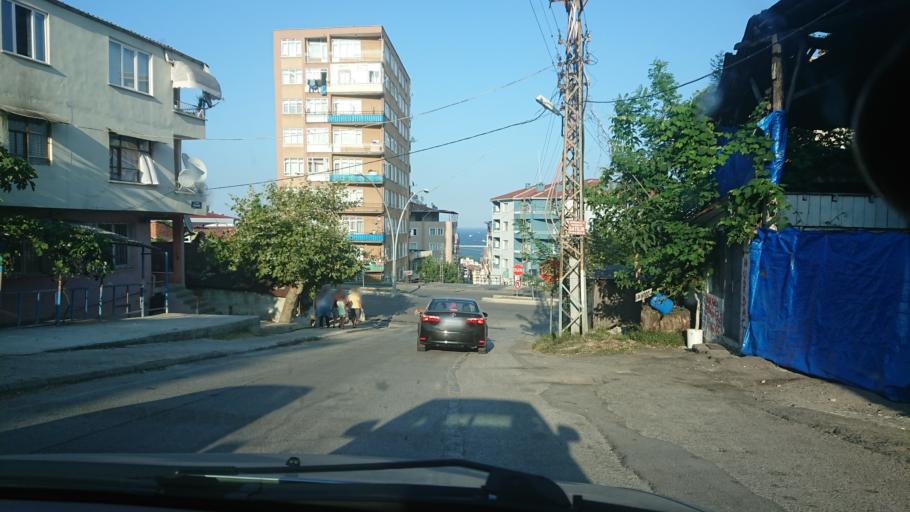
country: TR
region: Samsun
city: Samsun
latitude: 41.2969
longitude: 36.3227
